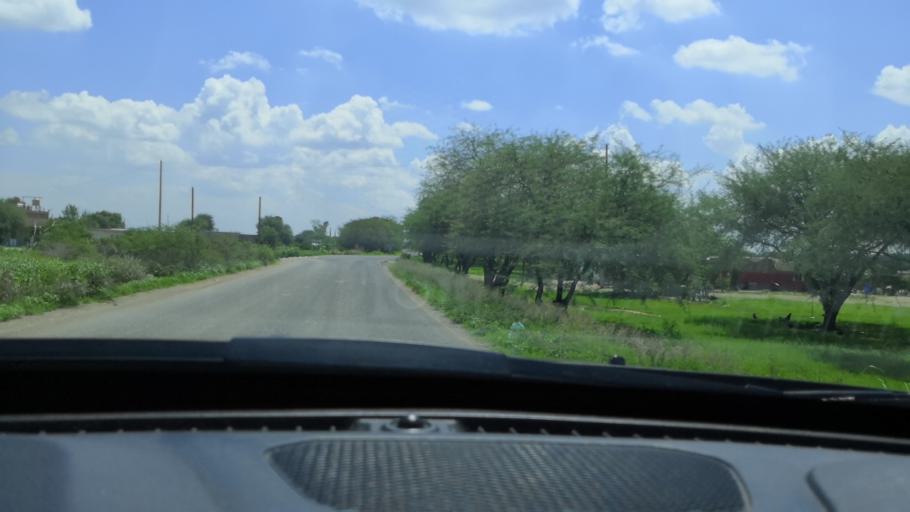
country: MX
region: Guanajuato
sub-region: Leon
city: Plan Guanajuato (La Sandia)
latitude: 20.9484
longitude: -101.6102
